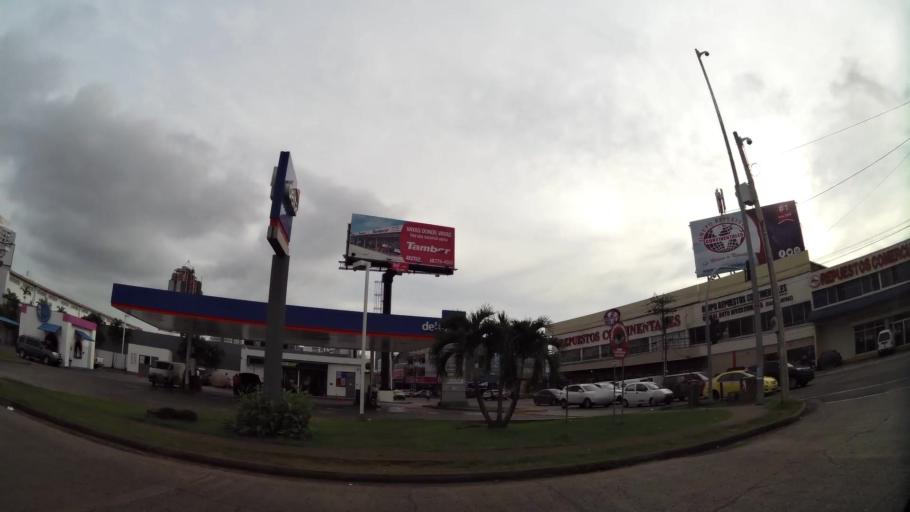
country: PA
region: Panama
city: Panama
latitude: 9.0013
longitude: -79.5198
